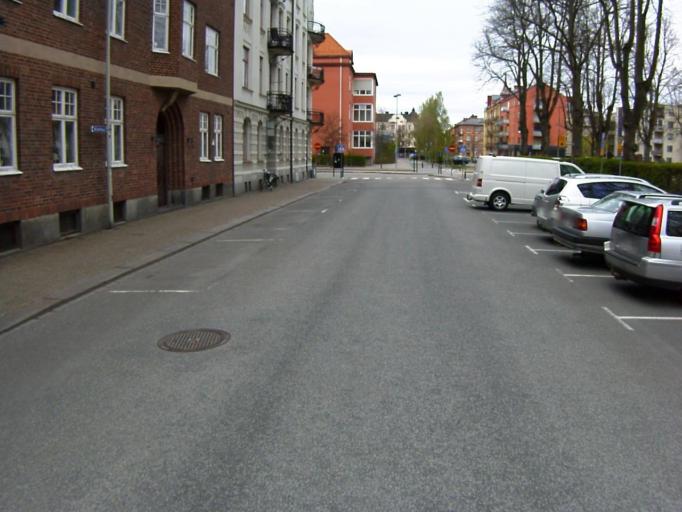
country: SE
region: Skane
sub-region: Kristianstads Kommun
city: Kristianstad
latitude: 56.0295
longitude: 14.1648
